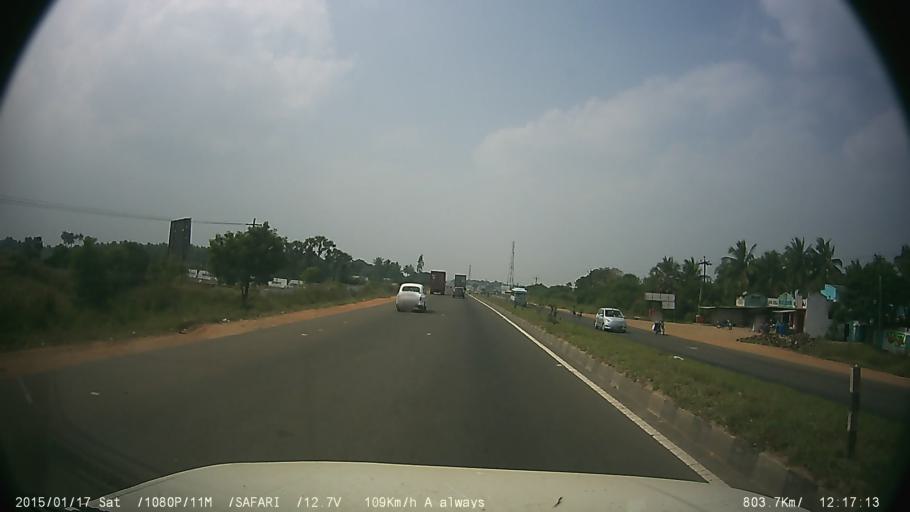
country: IN
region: Tamil Nadu
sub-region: Kancheepuram
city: Sriperumbudur
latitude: 12.9115
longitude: 79.8477
